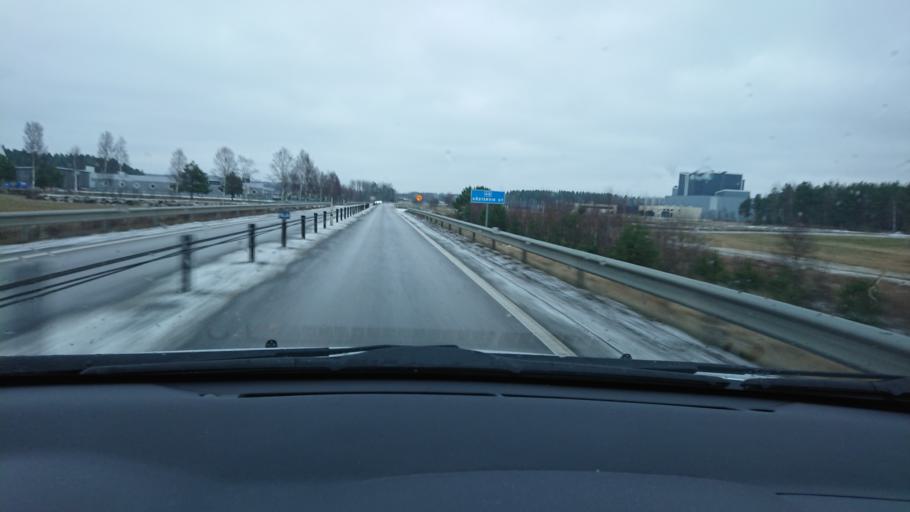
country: SE
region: Kalmar
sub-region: Vimmerby Kommun
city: Vimmerby
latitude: 57.6517
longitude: 15.8448
